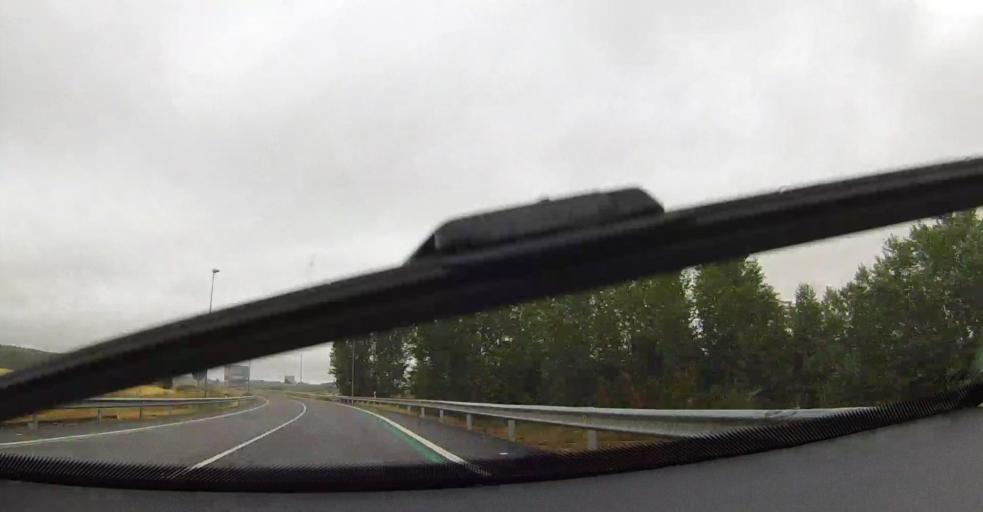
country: ES
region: Castille and Leon
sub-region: Provincia de Palencia
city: Carrion de los Condes
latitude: 42.3507
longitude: -4.6236
